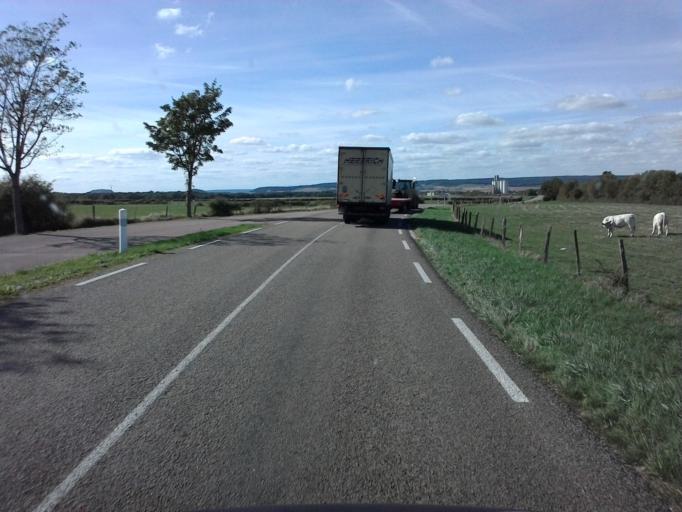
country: FR
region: Bourgogne
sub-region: Departement de la Cote-d'Or
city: Chatillon-sur-Seine
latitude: 47.9033
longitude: 4.6970
